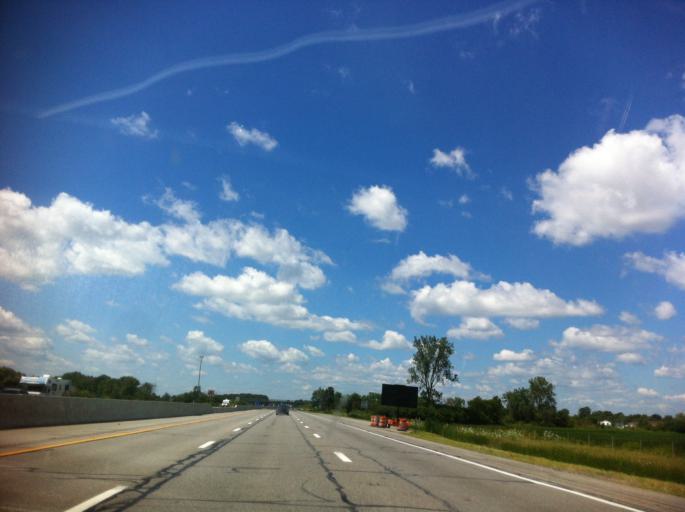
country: US
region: Ohio
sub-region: Wood County
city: Walbridge
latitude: 41.5452
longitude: -83.5297
